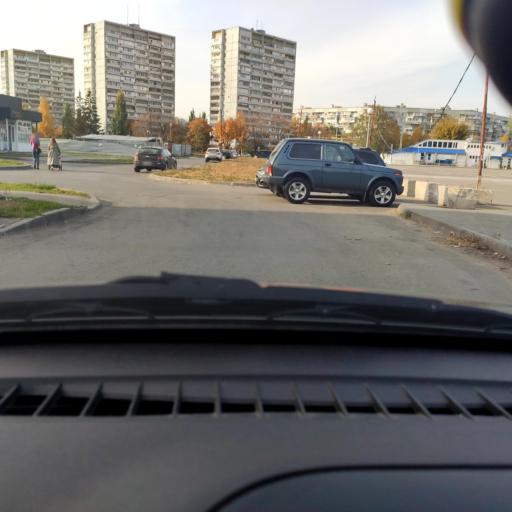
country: RU
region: Samara
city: Tol'yatti
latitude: 53.5305
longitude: 49.3440
